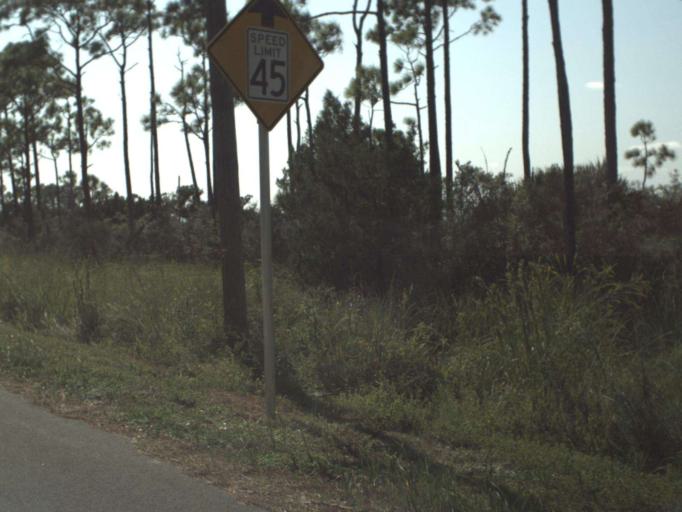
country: US
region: Florida
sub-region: Gulf County
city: Port Saint Joe
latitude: 29.7584
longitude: -85.3032
